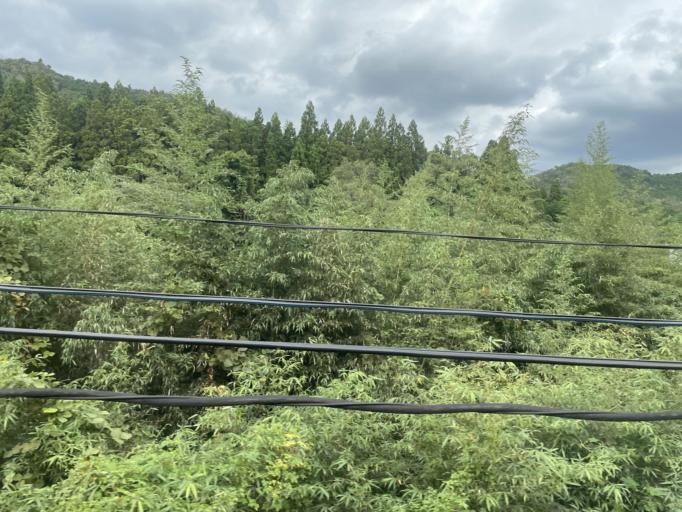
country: JP
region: Hyogo
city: Sasayama
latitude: 35.0797
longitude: 135.1473
